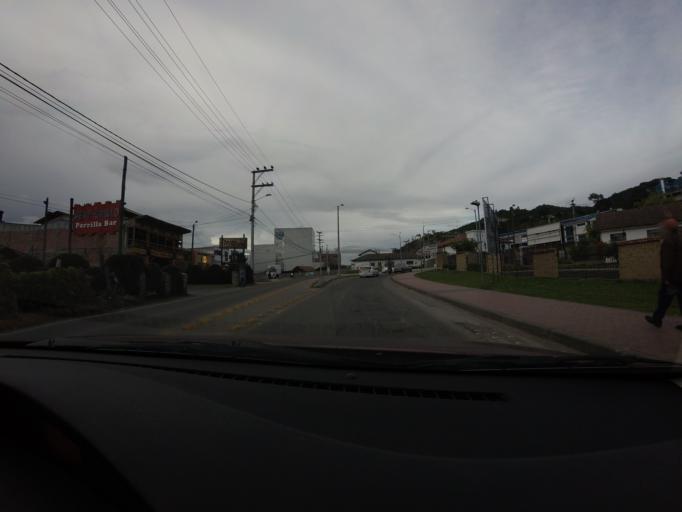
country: CO
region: Cundinamarca
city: Sopo
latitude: 4.9133
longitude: -73.9426
